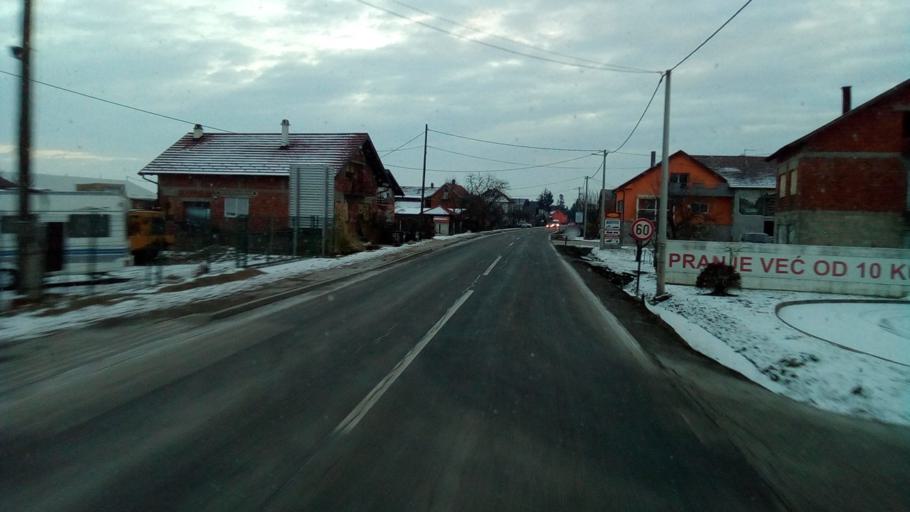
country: HR
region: Zagrebacka
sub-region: Grad Vrbovec
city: Vrbovec
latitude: 45.8762
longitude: 16.3710
